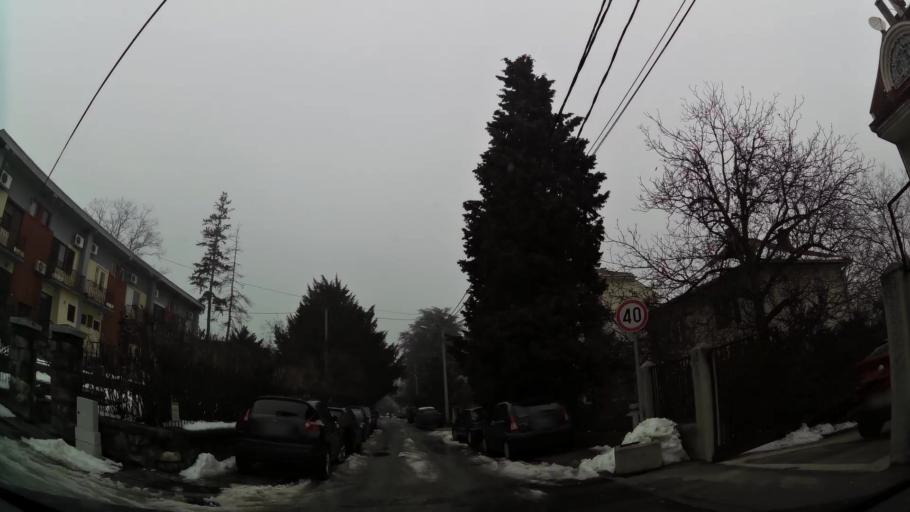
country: RS
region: Central Serbia
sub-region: Belgrade
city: Savski Venac
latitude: 44.7810
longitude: 20.4630
